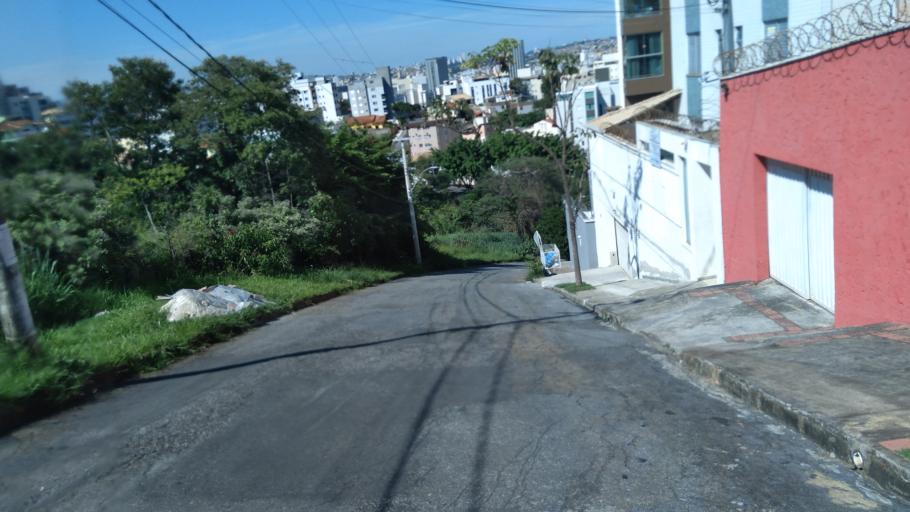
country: BR
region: Minas Gerais
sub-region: Belo Horizonte
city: Belo Horizonte
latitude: -19.8689
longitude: -43.9177
